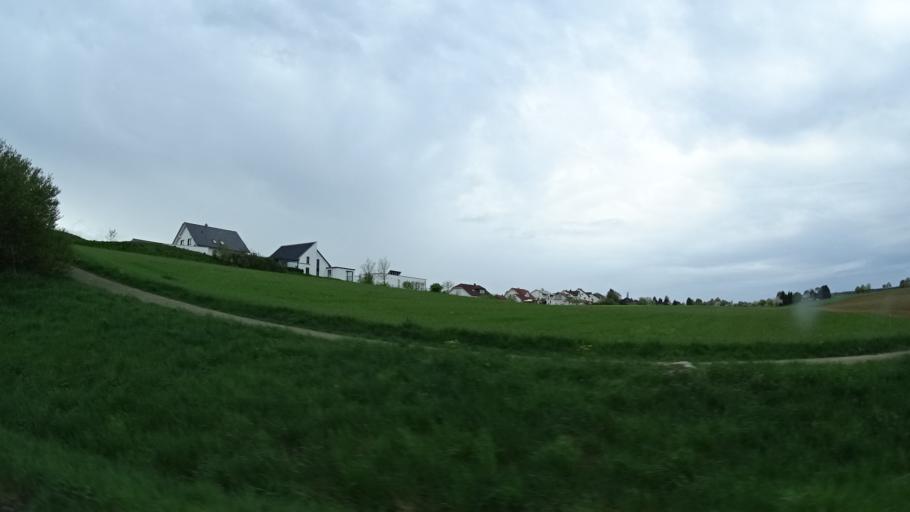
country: DE
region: Baden-Wuerttemberg
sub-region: Freiburg Region
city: Zimmern ob Rottweil
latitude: 48.1733
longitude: 8.6035
